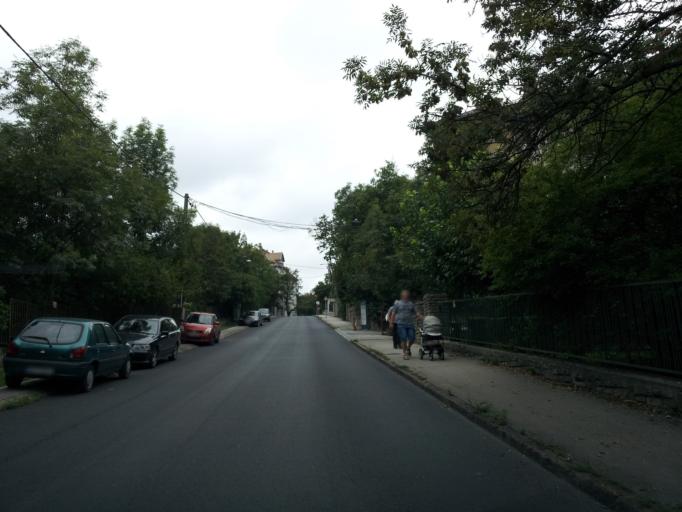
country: HU
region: Budapest
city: Budapest II. keruelet
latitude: 47.5129
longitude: 19.0202
